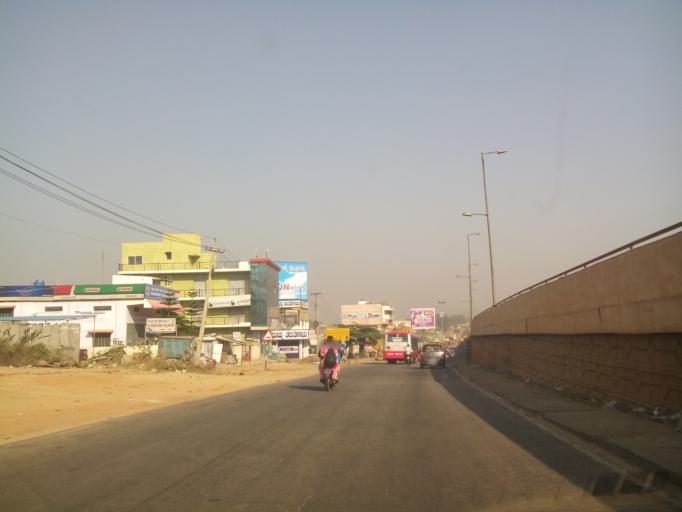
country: IN
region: Karnataka
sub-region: Bangalore Rural
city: Nelamangala
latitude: 13.0959
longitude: 77.3875
